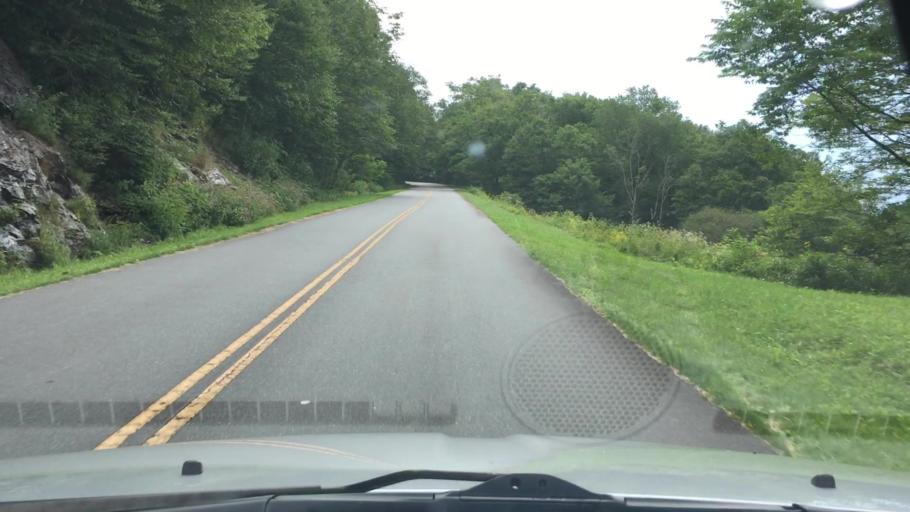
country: US
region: North Carolina
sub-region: Buncombe County
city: Swannanoa
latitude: 35.6947
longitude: -82.3901
